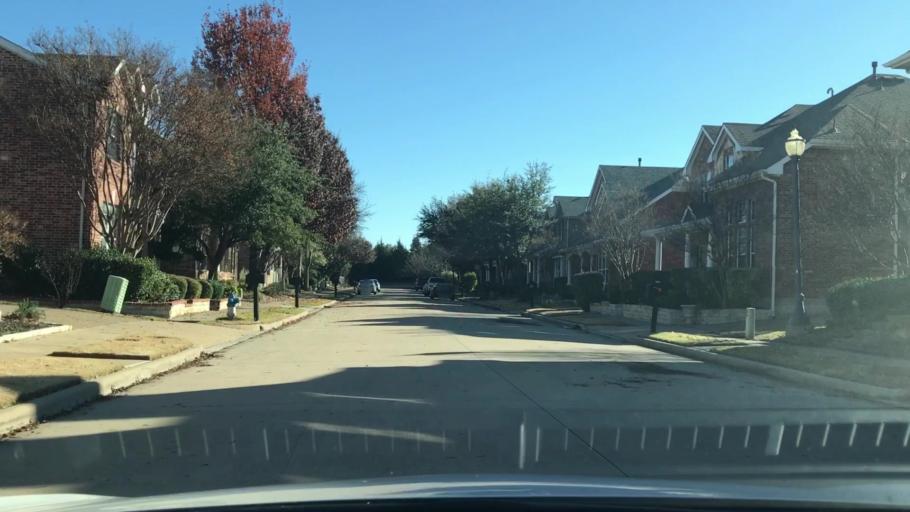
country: US
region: Texas
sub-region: Collin County
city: Frisco
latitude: 33.1156
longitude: -96.8502
